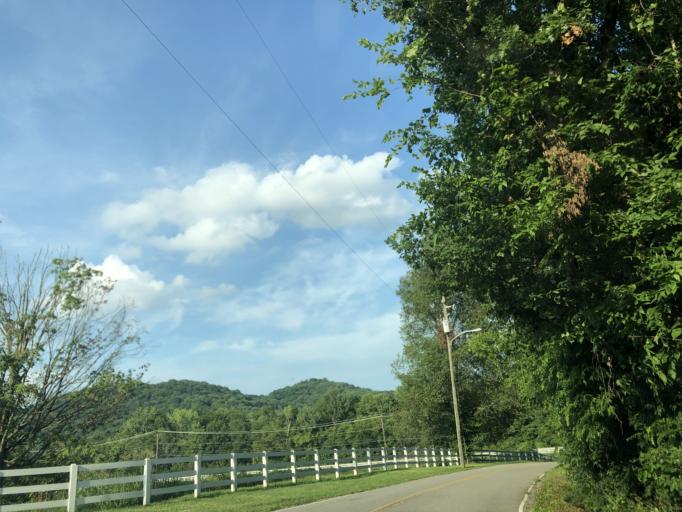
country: US
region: Tennessee
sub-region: Davidson County
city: Nashville
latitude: 36.2477
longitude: -86.8313
